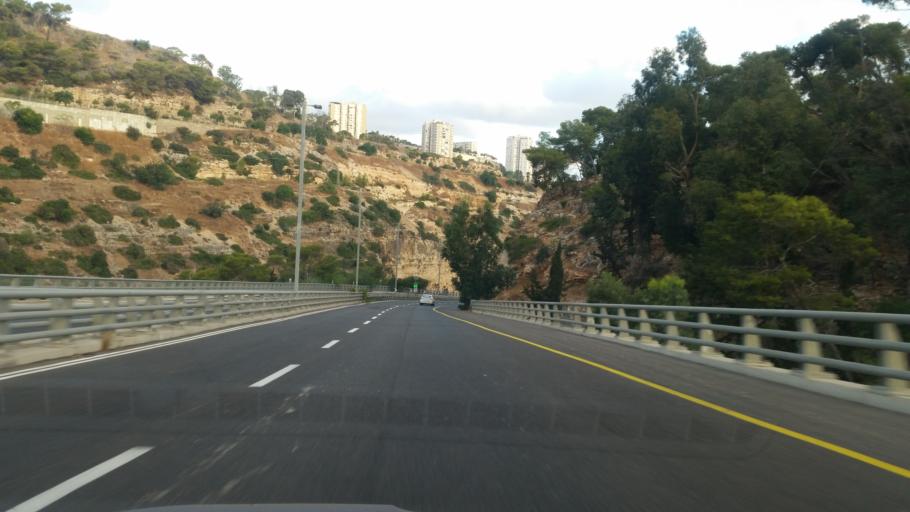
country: IL
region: Haifa
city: Haifa
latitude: 32.7928
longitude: 35.0051
